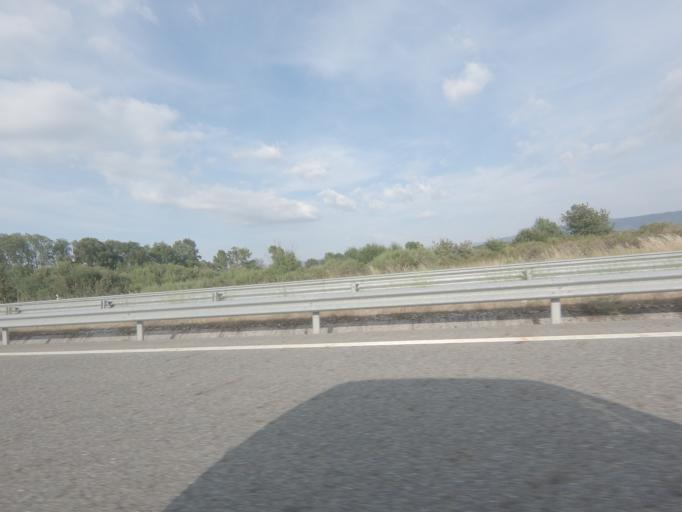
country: PT
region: Vila Real
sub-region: Chaves
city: Chaves
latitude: 41.7449
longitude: -7.5235
